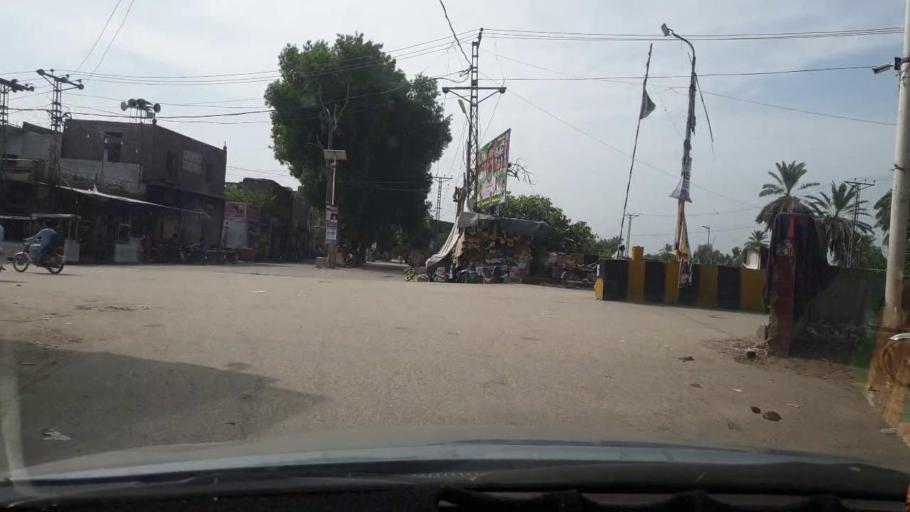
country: PK
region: Sindh
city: Khairpur
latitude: 27.5257
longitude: 68.7550
